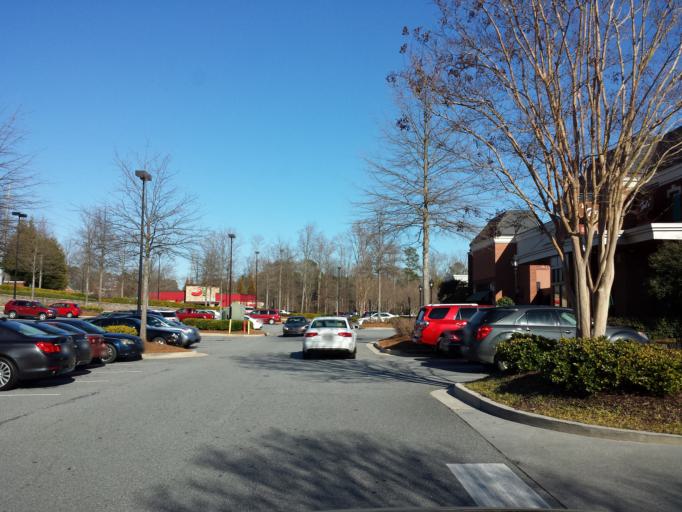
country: US
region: Georgia
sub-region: Cobb County
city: Kennesaw
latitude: 33.9528
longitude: -84.6577
